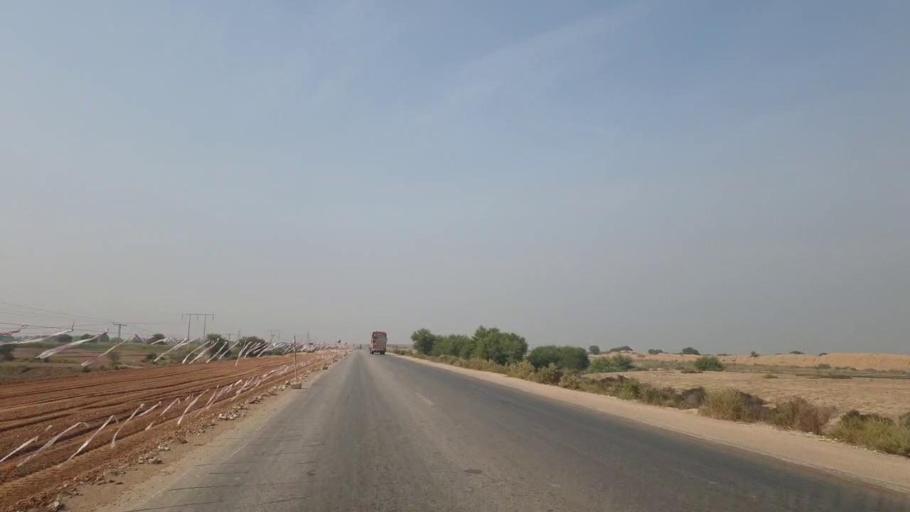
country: PK
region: Sindh
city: Sann
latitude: 26.1457
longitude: 68.0334
